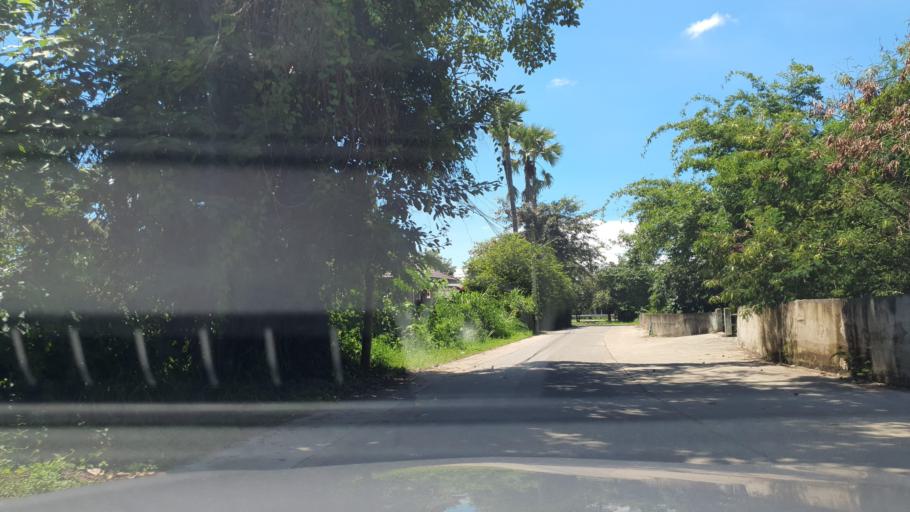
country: TH
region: Chiang Mai
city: San Kamphaeng
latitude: 18.7349
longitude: 99.1145
